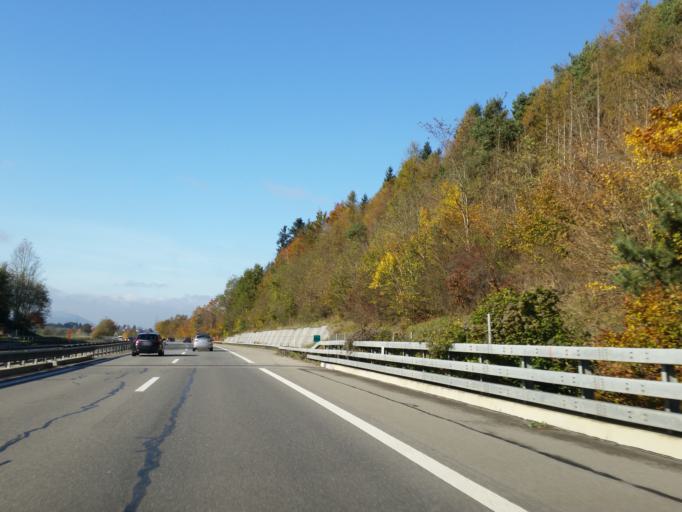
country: CH
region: Bern
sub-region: Bern-Mittelland District
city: Muhleberg
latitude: 46.9636
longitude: 7.2424
